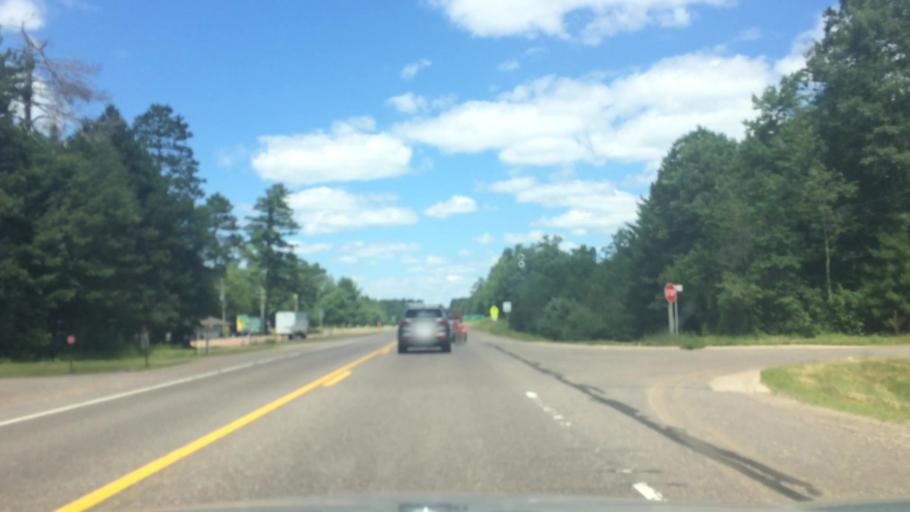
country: US
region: Wisconsin
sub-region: Vilas County
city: Lac du Flambeau
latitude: 45.9232
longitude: -89.6956
